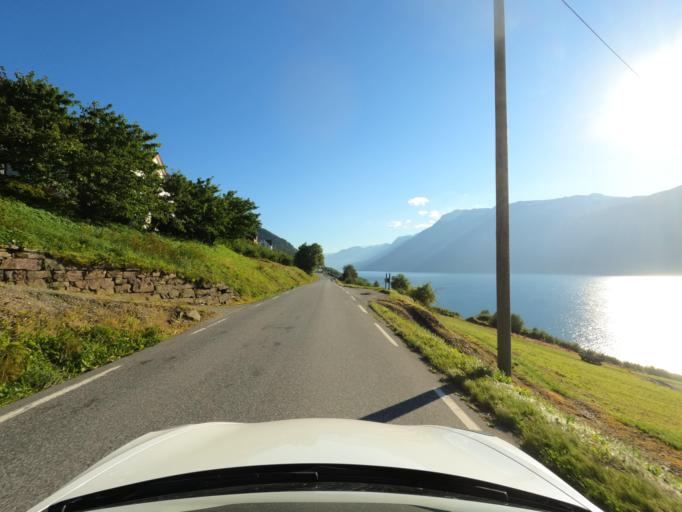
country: NO
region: Hordaland
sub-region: Ullensvang
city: Kinsarvik
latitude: 60.3739
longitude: 6.6828
